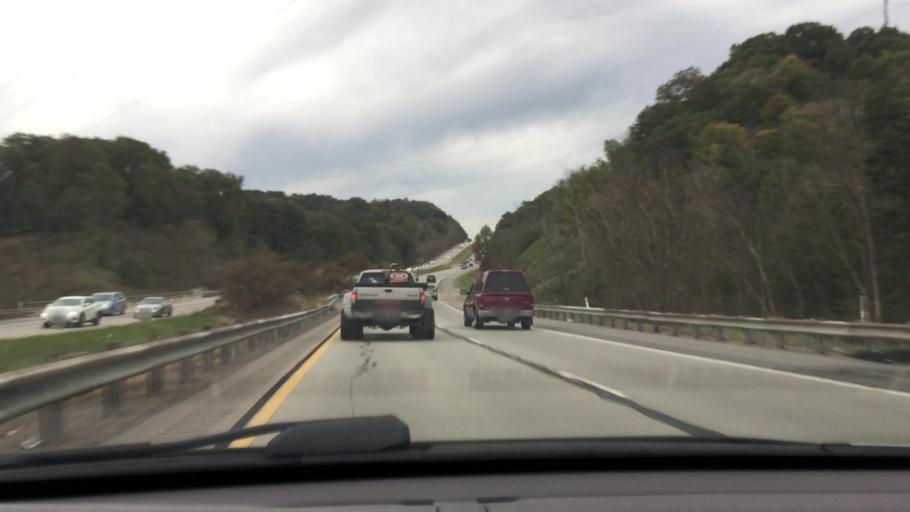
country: US
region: Pennsylvania
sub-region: Beaver County
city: Ambridge
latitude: 40.5779
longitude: -80.2890
